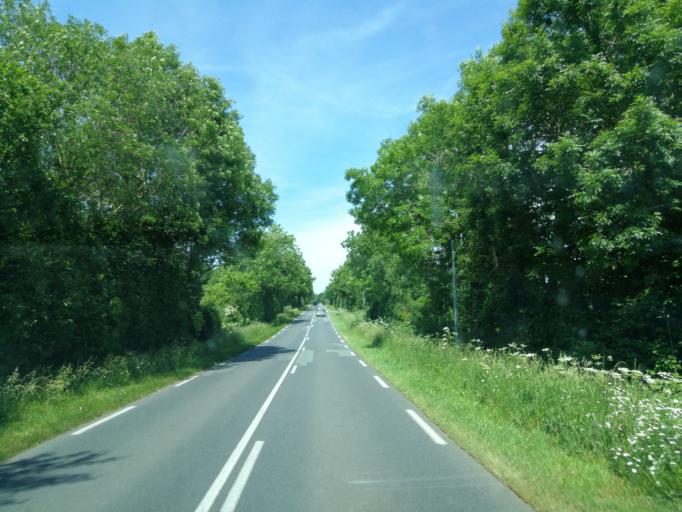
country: FR
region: Poitou-Charentes
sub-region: Departement des Deux-Sevres
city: La Foret-sur-Sevre
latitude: 46.7357
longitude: -0.6688
